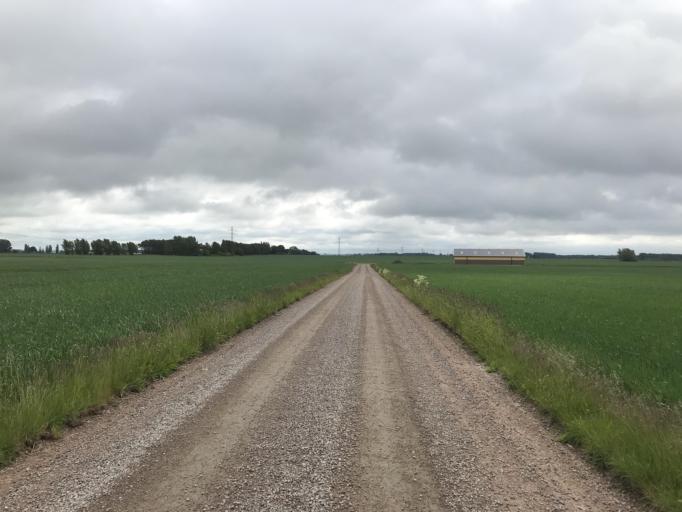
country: SE
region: Skane
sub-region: Landskrona
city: Asmundtorp
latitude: 55.8720
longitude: 12.8925
